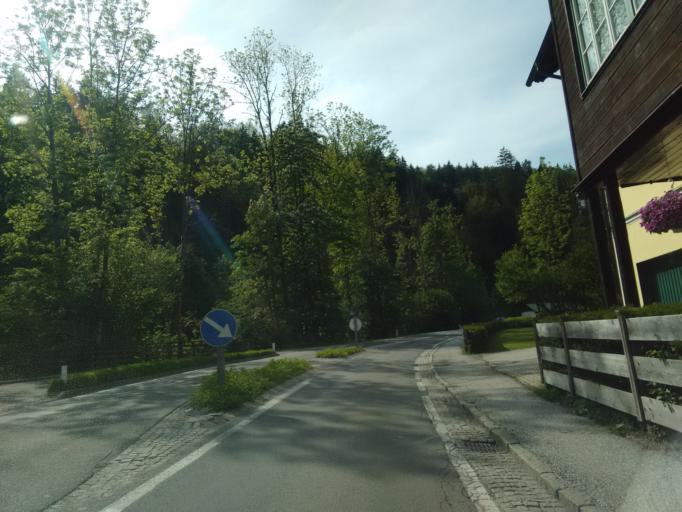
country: AT
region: Styria
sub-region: Politischer Bezirk Liezen
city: Bad Aussee
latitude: 47.6193
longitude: 13.7712
